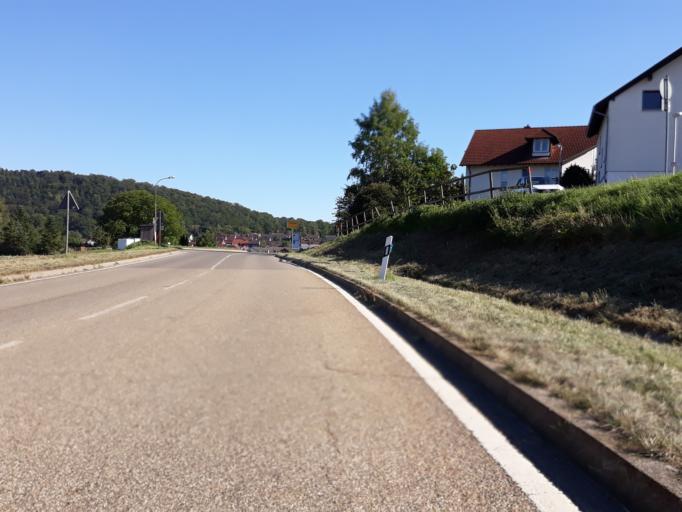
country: DE
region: Baden-Wuerttemberg
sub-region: Regierungsbezirk Stuttgart
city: Aidlingen
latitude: 48.6827
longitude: 8.9031
